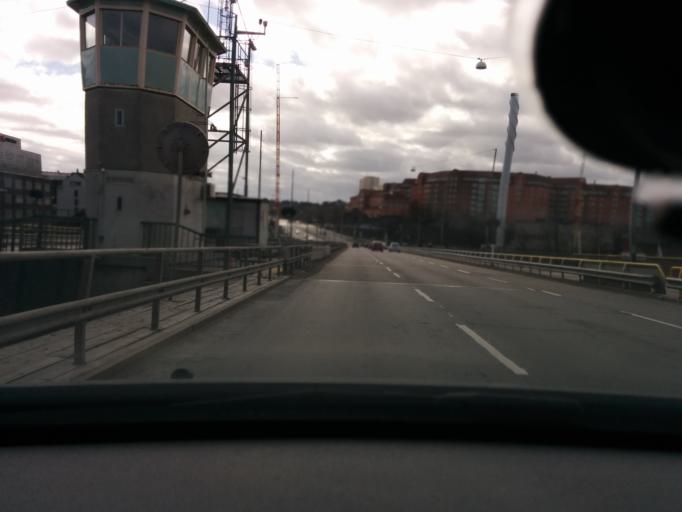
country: SE
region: Stockholm
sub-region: Stockholms Kommun
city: Arsta
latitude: 59.3133
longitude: 18.0318
